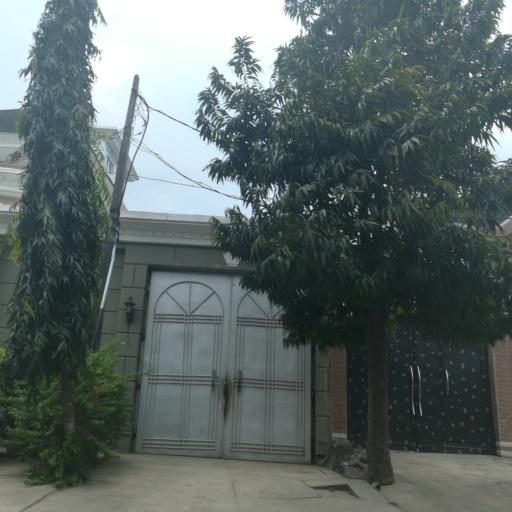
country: NG
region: Lagos
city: Ojota
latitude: 6.5764
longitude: 3.3874
